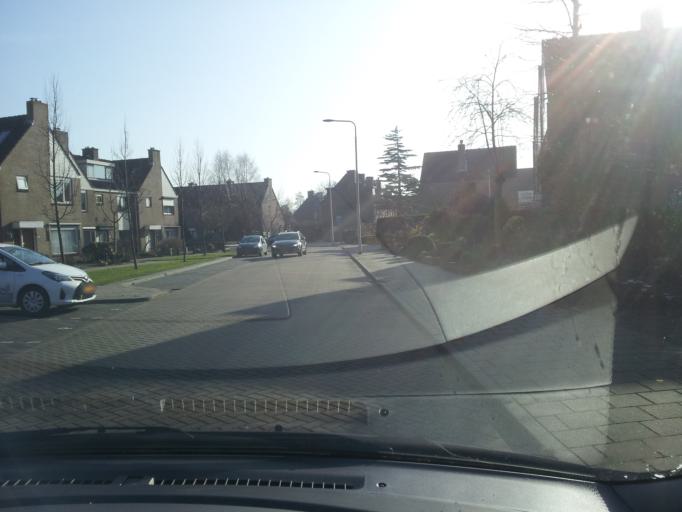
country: NL
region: South Holland
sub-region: Gemeente Den Haag
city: Ypenburg
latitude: 52.0462
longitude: 4.3975
